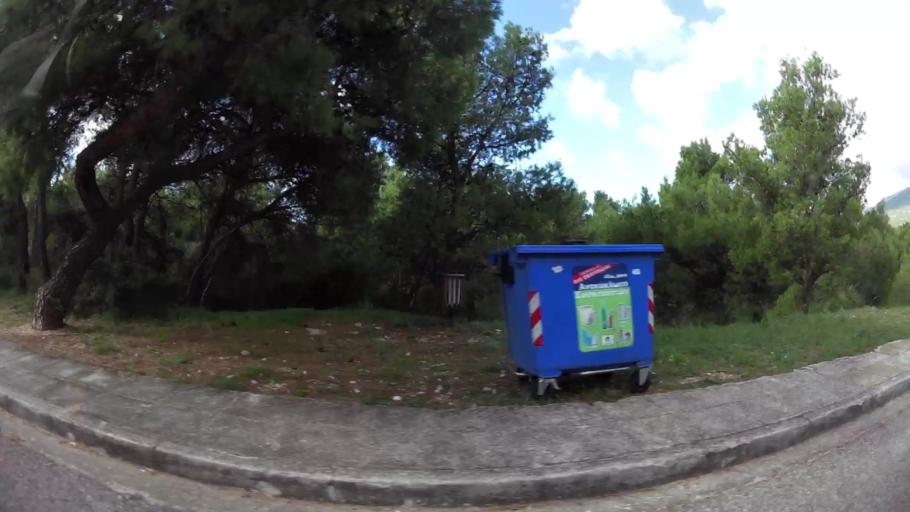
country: GR
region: Attica
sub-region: Nomarchia Anatolikis Attikis
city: Thrakomakedones
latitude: 38.1231
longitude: 23.7519
